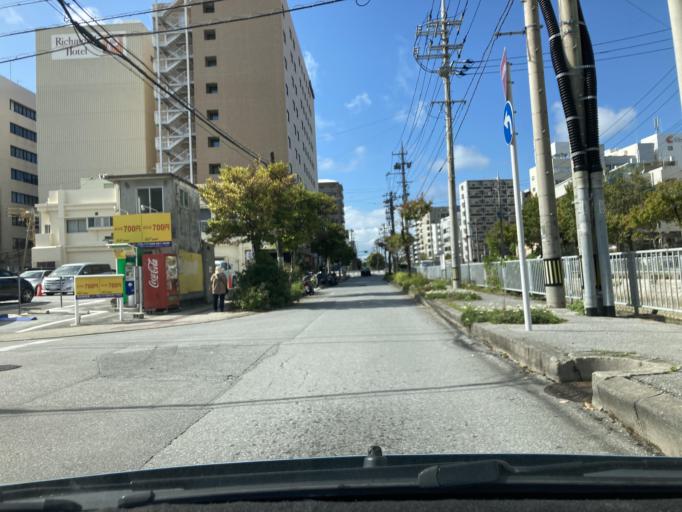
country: JP
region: Okinawa
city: Naha-shi
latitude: 26.2201
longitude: 127.6837
